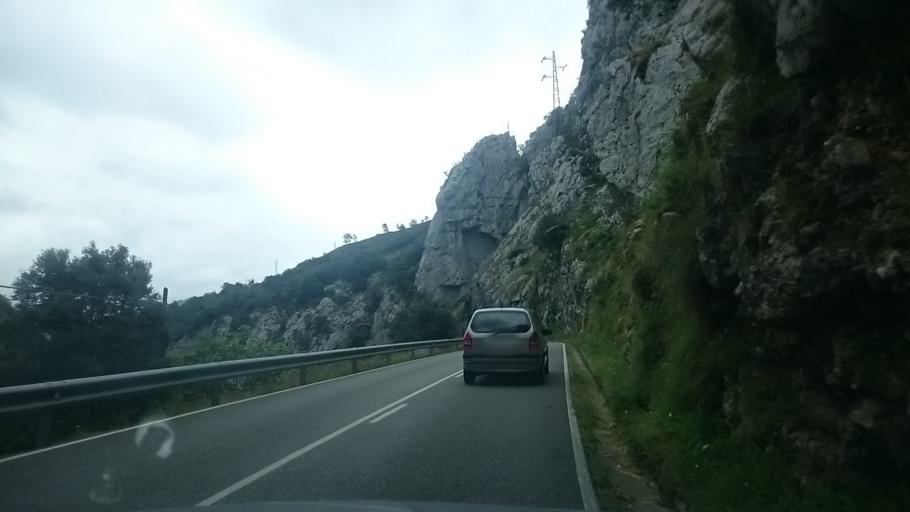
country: ES
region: Asturias
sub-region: Province of Asturias
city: Carrena
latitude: 43.2885
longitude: -4.8288
